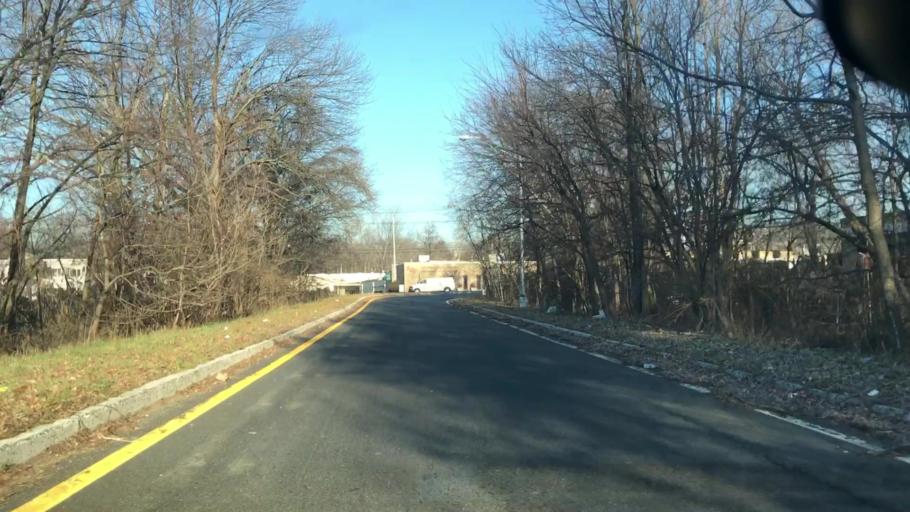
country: US
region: New Jersey
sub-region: Passaic County
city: Totowa
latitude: 40.8977
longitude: -74.2199
